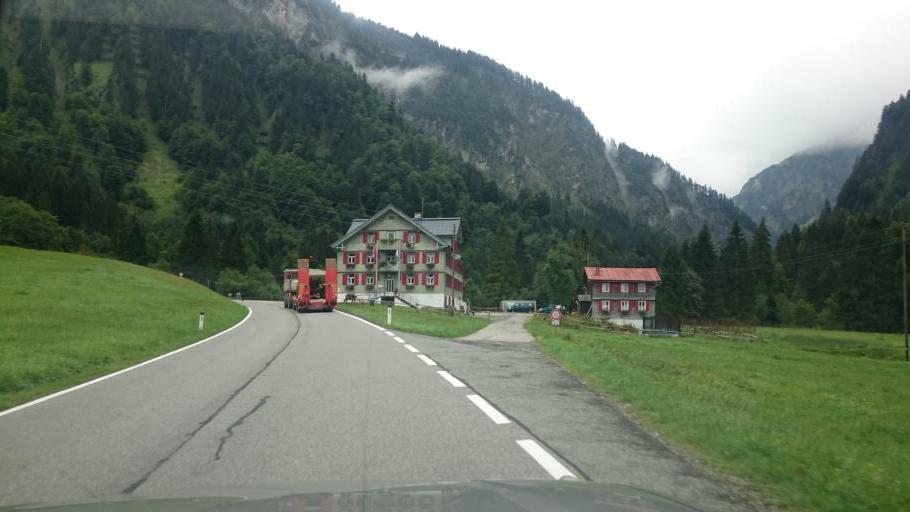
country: AT
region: Vorarlberg
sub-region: Politischer Bezirk Bregenz
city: Schroecken
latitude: 47.2823
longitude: 10.0570
